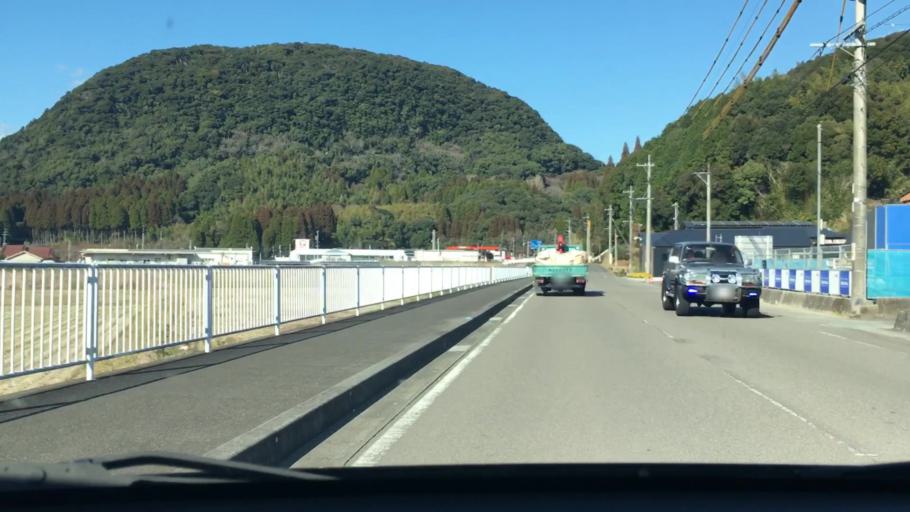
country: JP
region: Kagoshima
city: Satsumasendai
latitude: 31.7943
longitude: 130.4103
